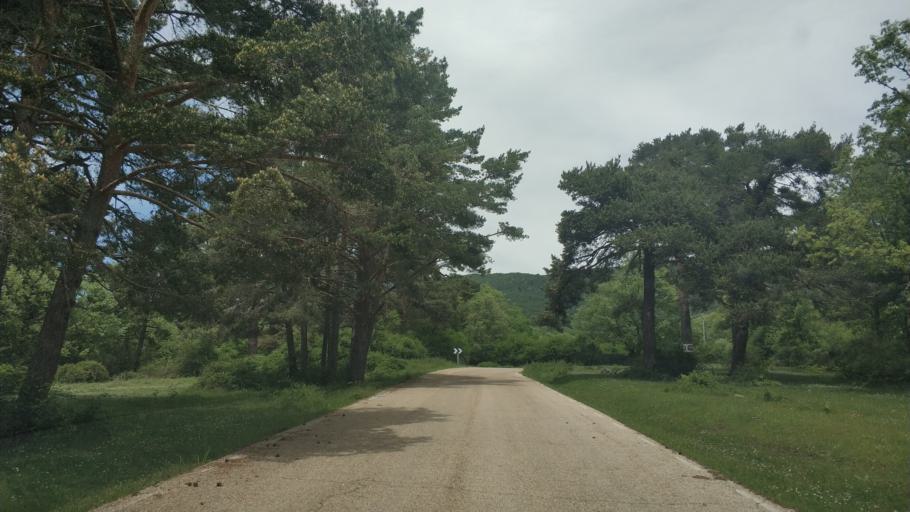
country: ES
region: Castille and Leon
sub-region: Provincia de Soria
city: Vinuesa
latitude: 41.9701
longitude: -2.7807
